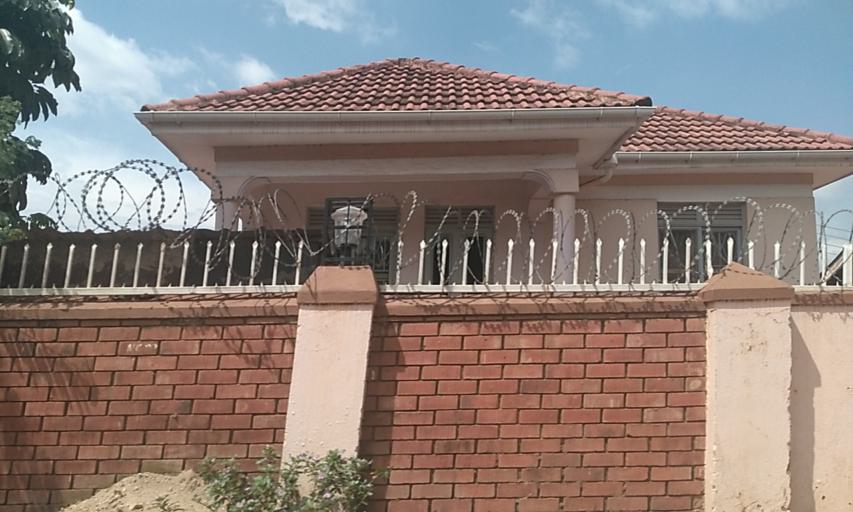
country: UG
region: Central Region
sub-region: Wakiso District
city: Kireka
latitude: 0.3505
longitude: 32.6142
